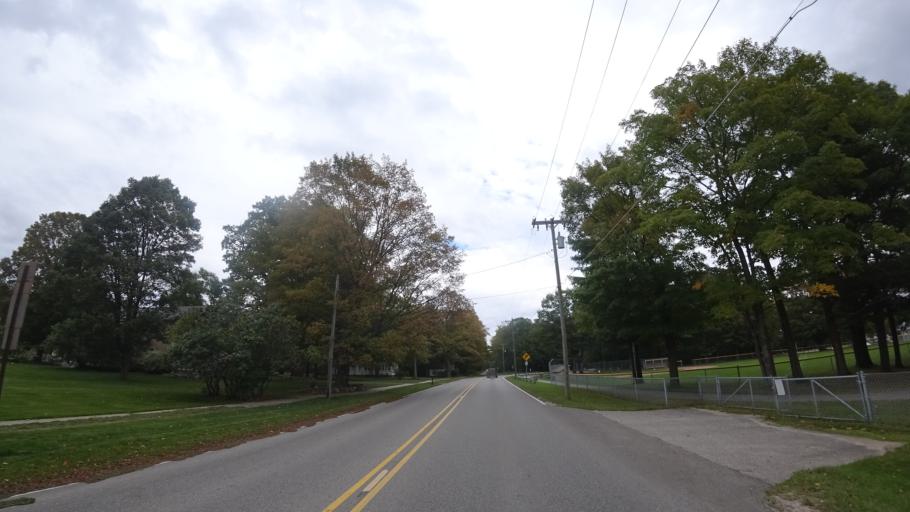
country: US
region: Michigan
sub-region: Emmet County
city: Harbor Springs
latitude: 45.4354
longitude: -84.9746
